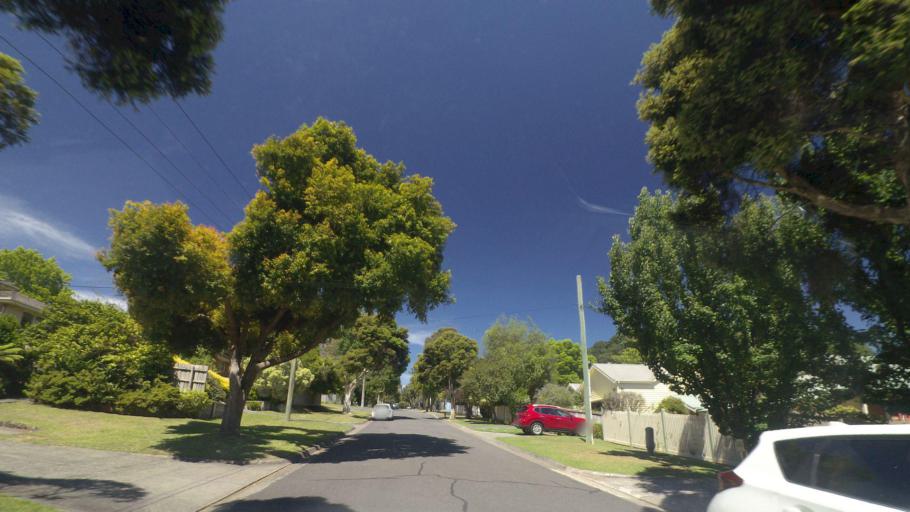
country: AU
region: Victoria
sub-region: Maroondah
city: Ringwood East
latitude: -37.8000
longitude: 145.2304
